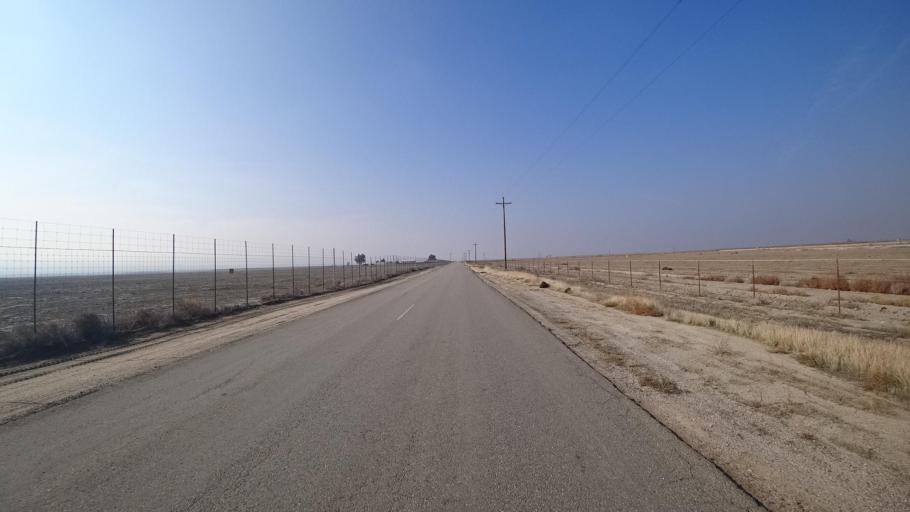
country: US
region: California
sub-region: Kern County
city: Buttonwillow
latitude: 35.3331
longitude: -119.3672
